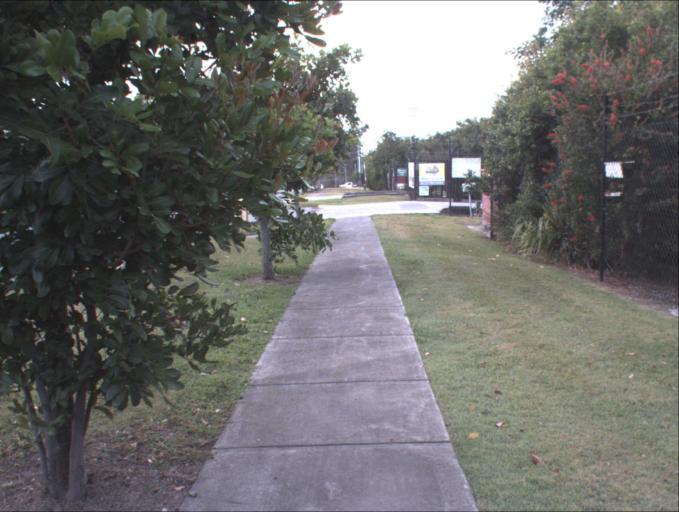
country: AU
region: Queensland
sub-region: Logan
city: Waterford West
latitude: -27.6669
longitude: 153.1247
